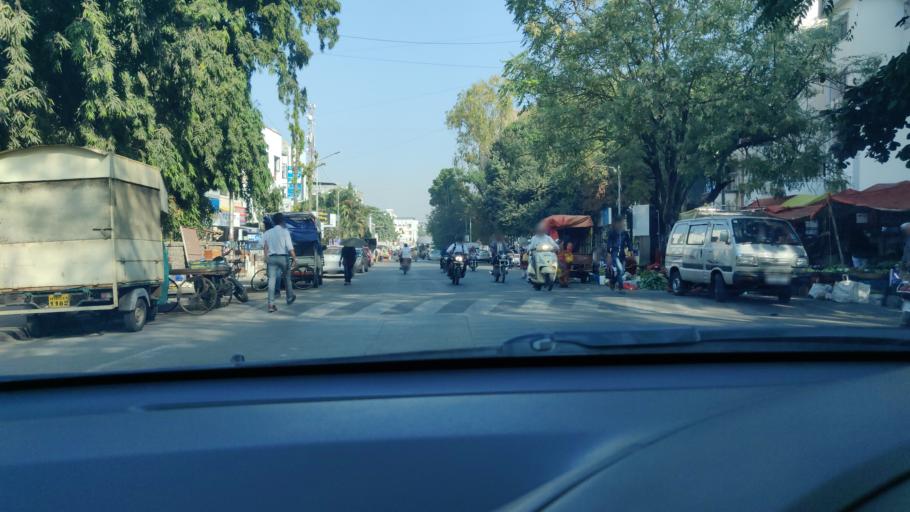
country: IN
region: Maharashtra
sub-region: Pune Division
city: Khadki
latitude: 18.5588
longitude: 73.8036
